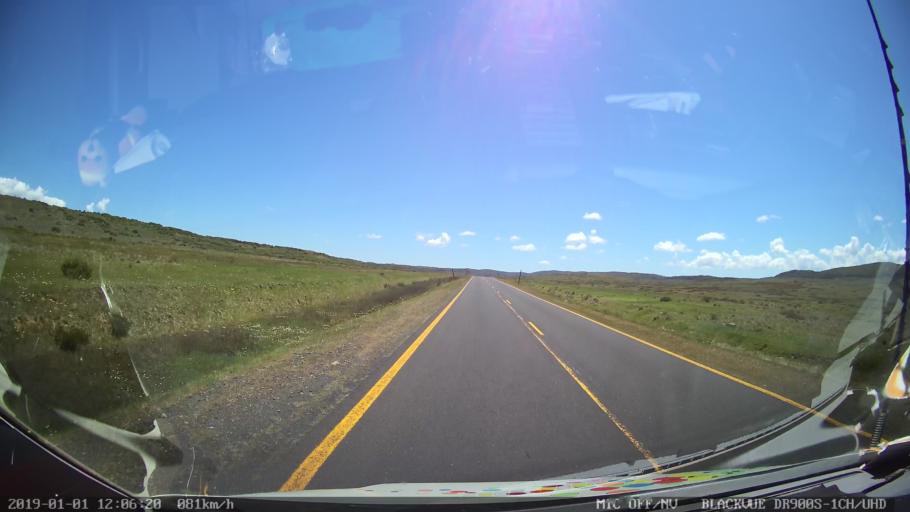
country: AU
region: New South Wales
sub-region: Snowy River
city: Jindabyne
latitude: -35.8462
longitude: 148.4913
